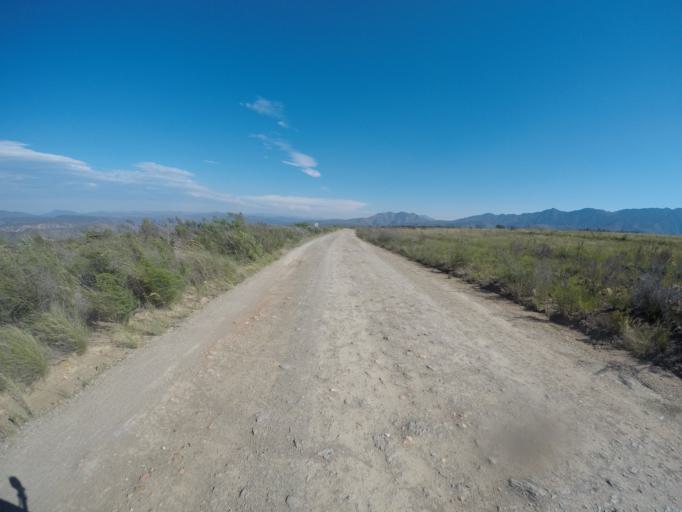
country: ZA
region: Eastern Cape
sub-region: Cacadu District Municipality
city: Kareedouw
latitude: -33.6341
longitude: 24.4804
